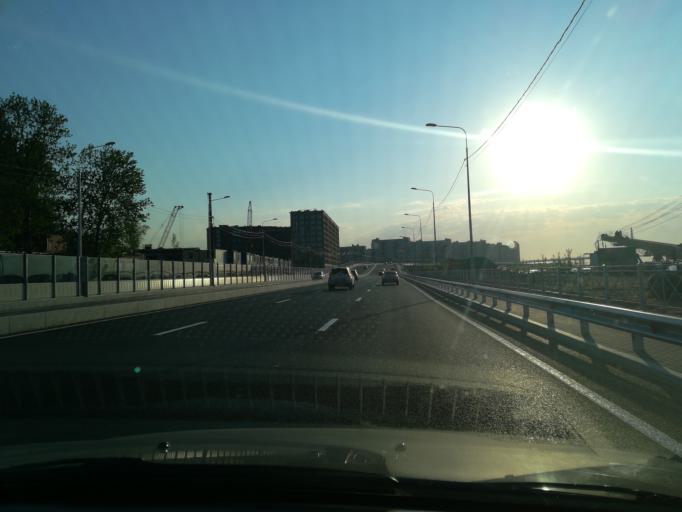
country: RU
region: Leningrad
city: Krestovskiy ostrov
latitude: 59.9579
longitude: 30.2495
